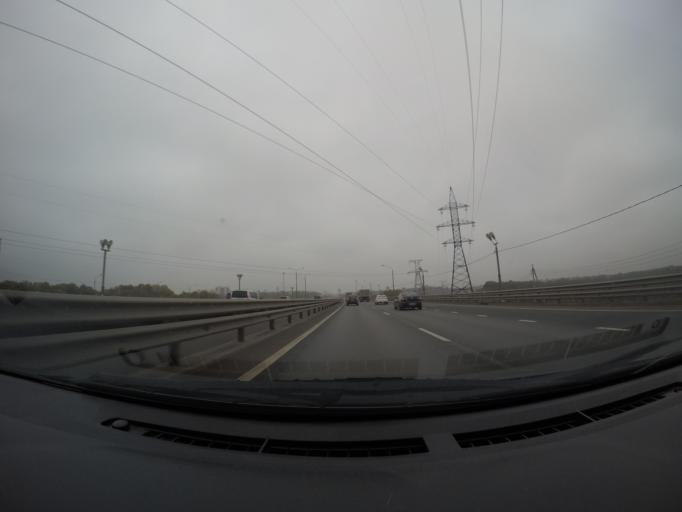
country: RU
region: Moskovskaya
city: Shcherbinka
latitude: 55.4635
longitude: 37.6187
